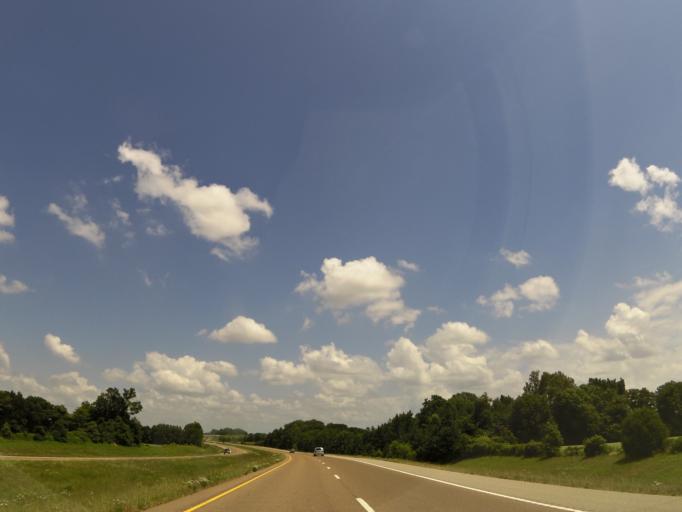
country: US
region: Tennessee
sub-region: Crockett County
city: Alamo
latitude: 35.7796
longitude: -89.1389
